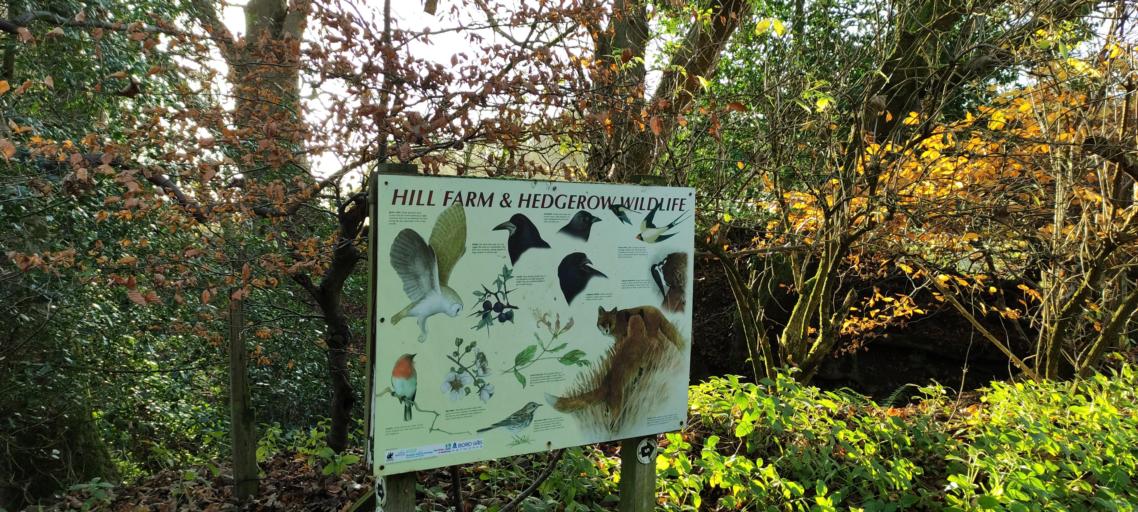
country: GB
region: Scotland
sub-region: Dumfries and Galloway
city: Langholm
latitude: 55.1489
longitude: -3.0042
